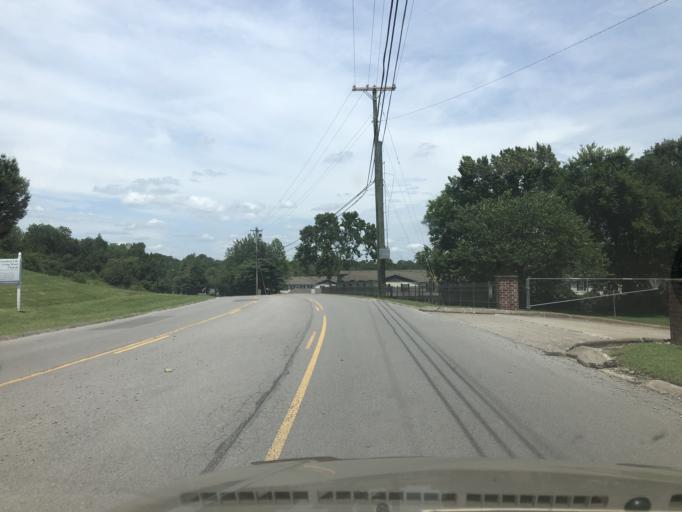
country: US
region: Tennessee
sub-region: Davidson County
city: Lakewood
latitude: 36.2555
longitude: -86.6734
